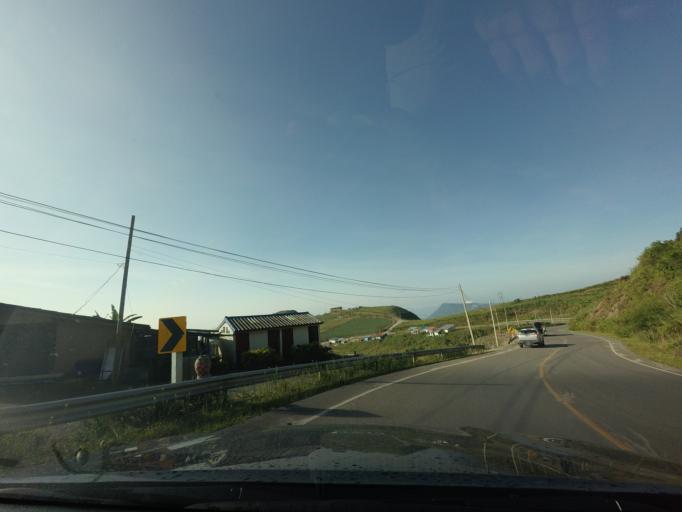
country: TH
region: Phetchabun
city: Lom Kao
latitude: 16.8902
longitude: 101.0969
